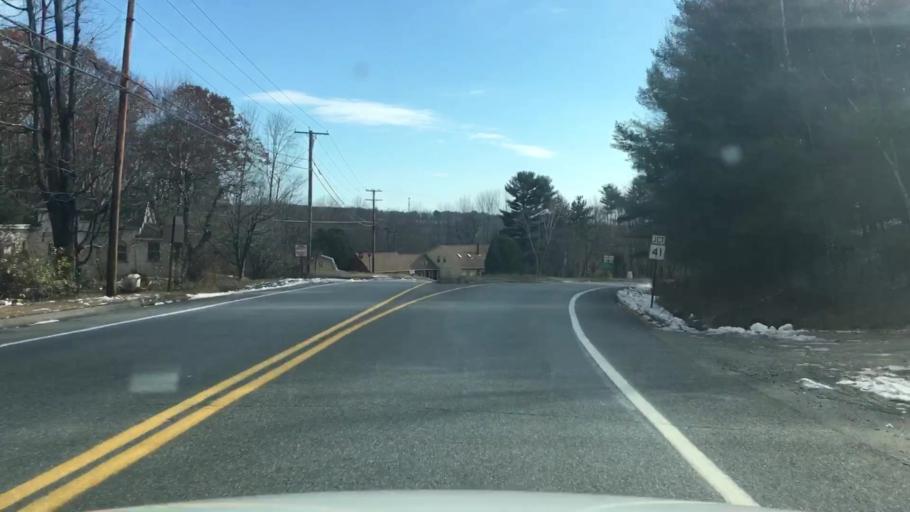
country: US
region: Maine
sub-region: Kennebec County
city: Winthrop
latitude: 44.3218
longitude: -69.9804
